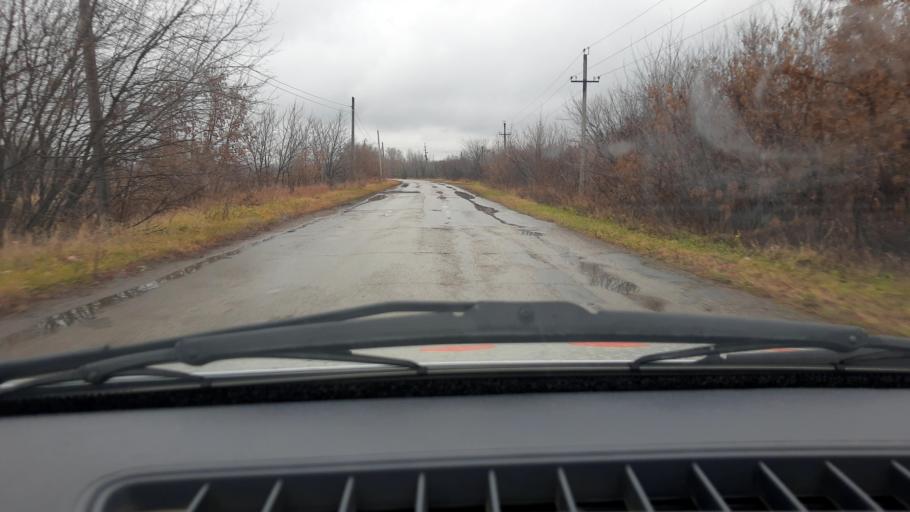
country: RU
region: Bashkortostan
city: Iglino
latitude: 54.8032
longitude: 56.1947
